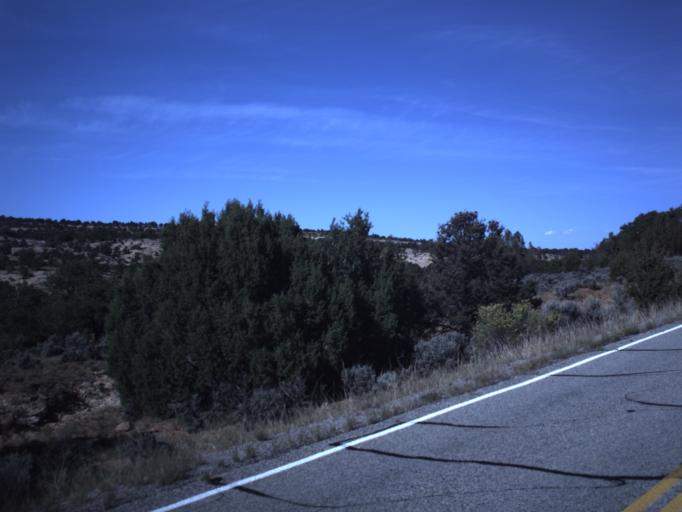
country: US
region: Utah
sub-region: San Juan County
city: Monticello
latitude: 37.9923
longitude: -109.4886
